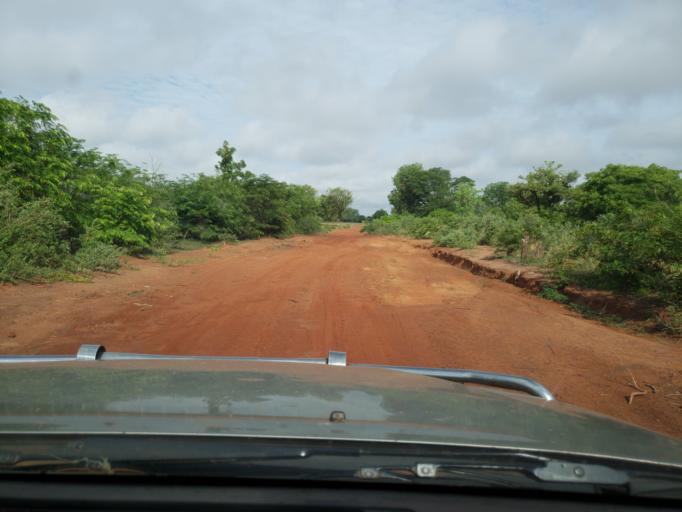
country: ML
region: Sikasso
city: Koutiala
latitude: 12.3925
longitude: -5.9864
